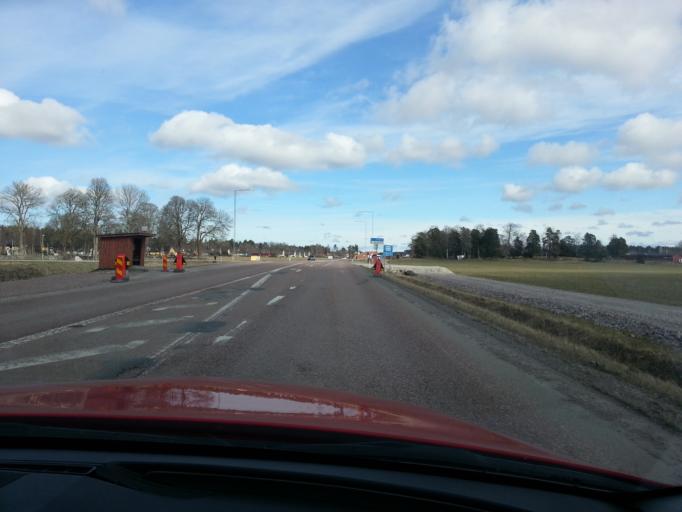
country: SE
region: Uppsala
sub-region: Osthammars Kommun
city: Gimo
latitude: 60.0579
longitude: 18.0669
